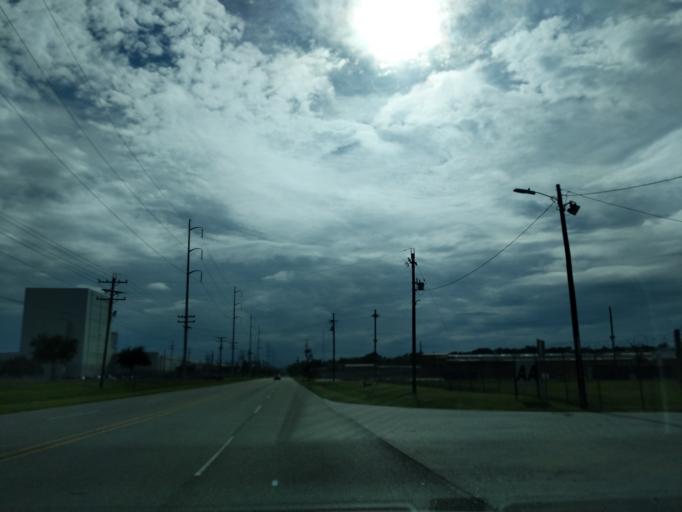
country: US
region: Louisiana
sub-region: Saint Bernard Parish
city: Chalmette
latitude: 30.0311
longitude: -89.9126
